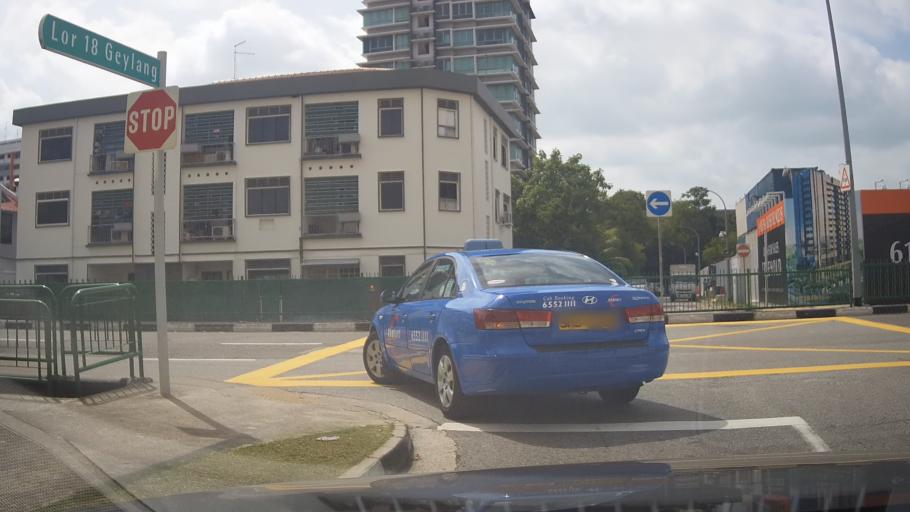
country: SG
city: Singapore
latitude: 1.3104
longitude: 103.8808
